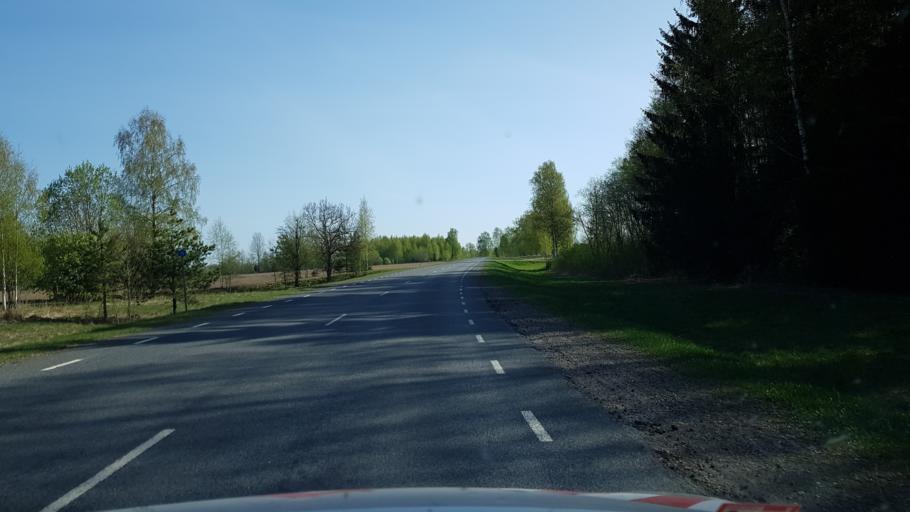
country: EE
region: Viljandimaa
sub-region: Abja vald
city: Abja-Paluoja
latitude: 58.1491
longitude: 25.4028
